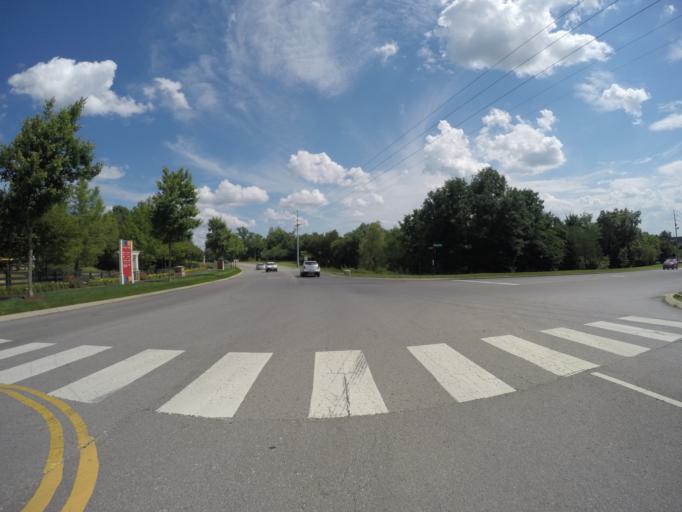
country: US
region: Tennessee
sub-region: Wilson County
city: Mount Juliet
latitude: 36.1633
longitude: -86.5033
